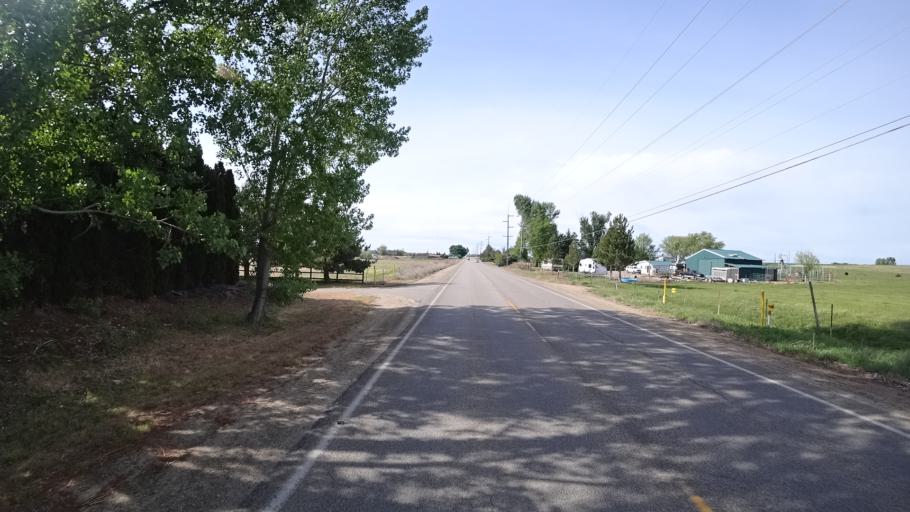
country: US
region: Idaho
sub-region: Ada County
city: Kuna
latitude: 43.5227
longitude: -116.3344
